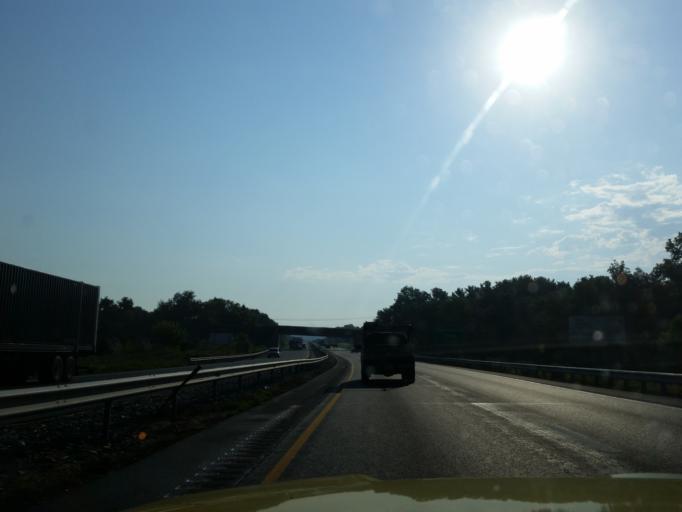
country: US
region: Pennsylvania
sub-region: Lancaster County
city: Mountville
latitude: 40.0465
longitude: -76.4144
